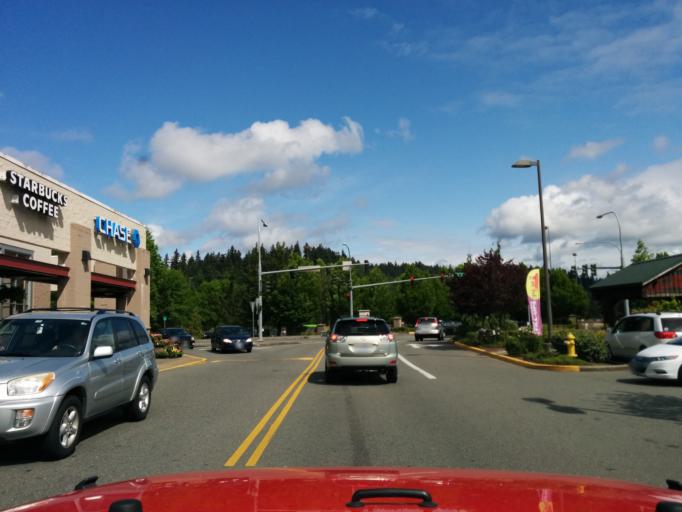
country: US
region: Washington
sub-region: King County
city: Redmond
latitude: 47.6710
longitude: -122.1042
